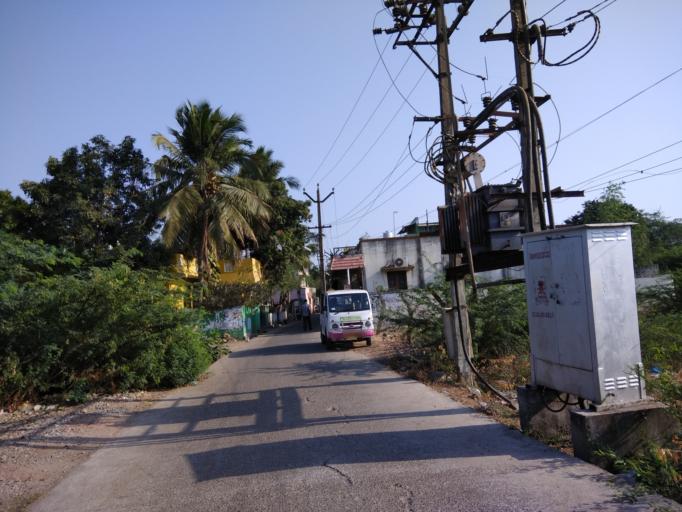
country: IN
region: Tamil Nadu
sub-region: Kancheepuram
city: Saint Thomas Mount
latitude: 13.0113
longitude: 80.1864
